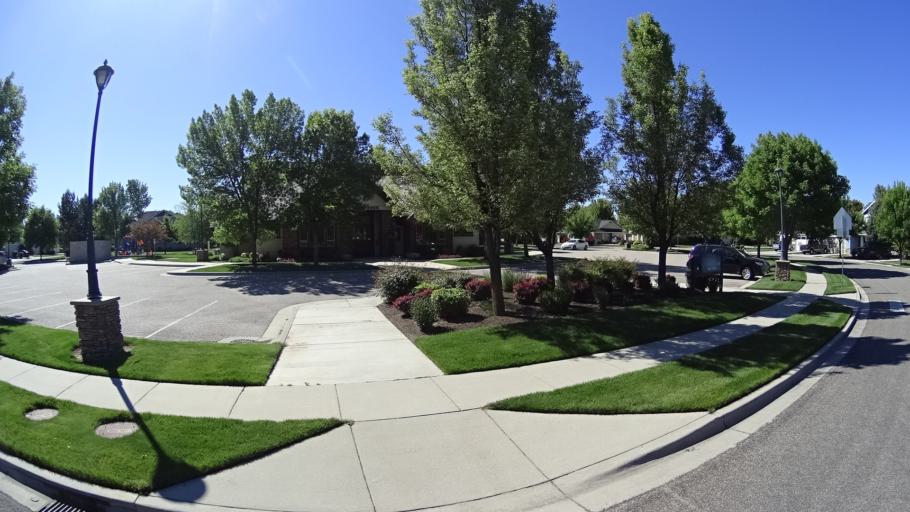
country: US
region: Idaho
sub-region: Ada County
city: Meridian
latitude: 43.6566
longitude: -116.4047
